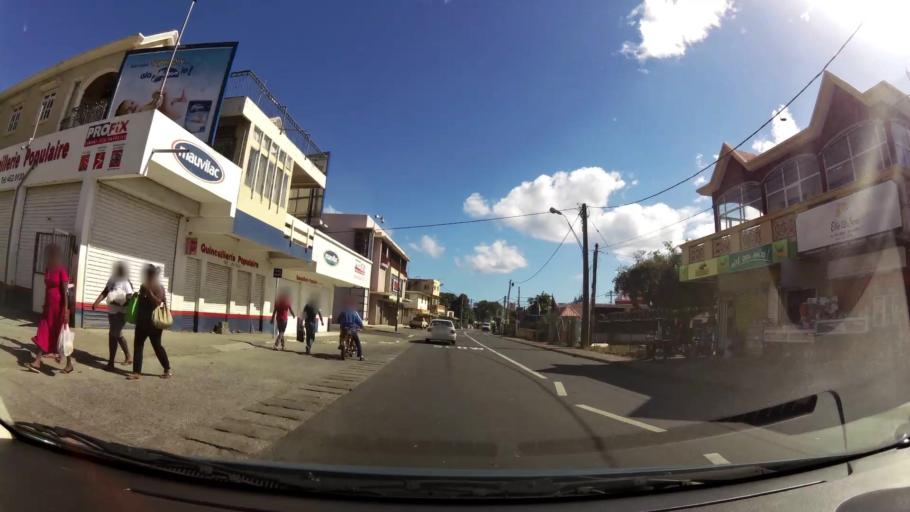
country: MU
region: Black River
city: Cascavelle
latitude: -20.2572
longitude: 57.4142
